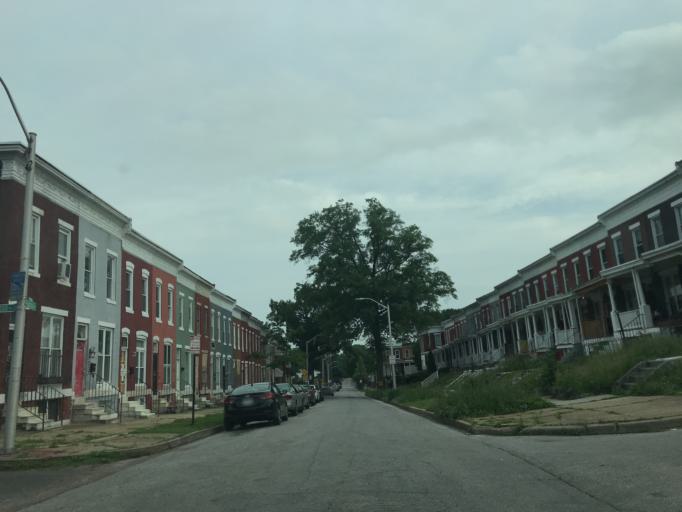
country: US
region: Maryland
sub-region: City of Baltimore
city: Baltimore
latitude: 39.3086
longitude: -76.6610
